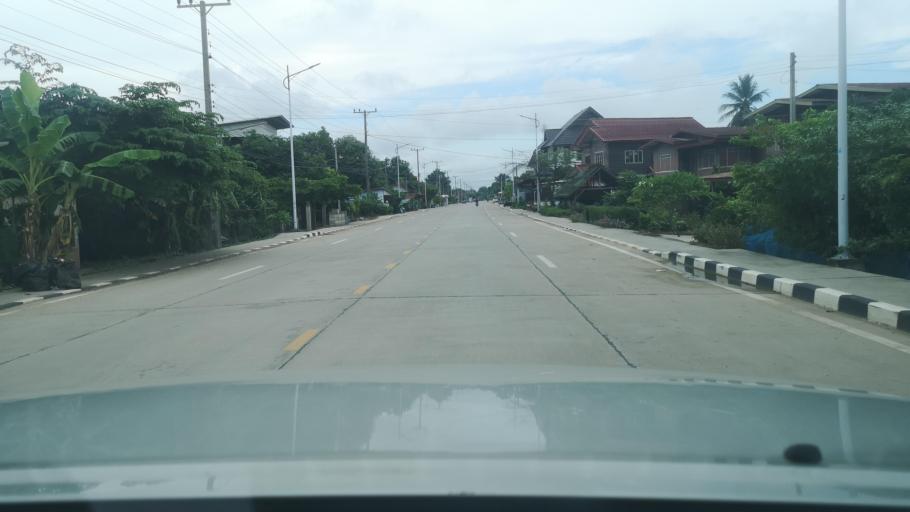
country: TH
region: Nong Khai
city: Tha Bo
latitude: 17.8300
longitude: 102.6483
